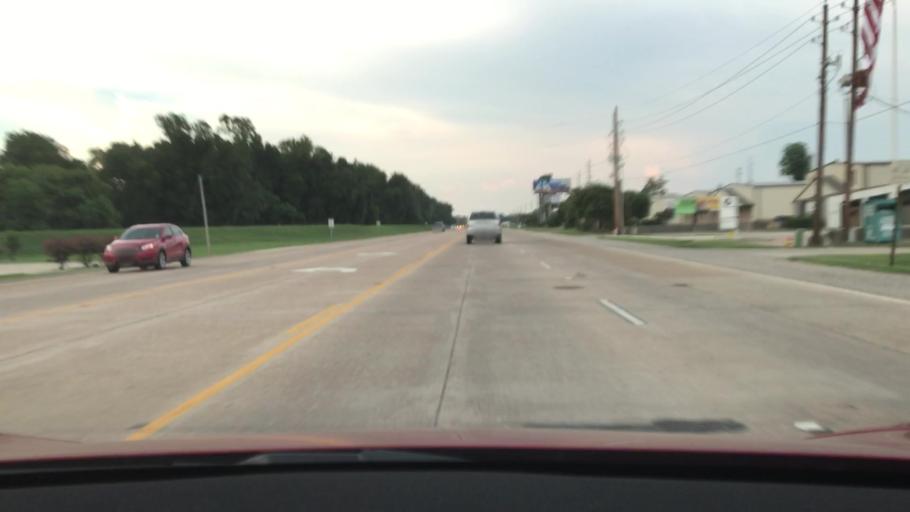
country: US
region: Louisiana
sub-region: Bossier Parish
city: Bossier City
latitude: 32.4501
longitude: -93.6968
